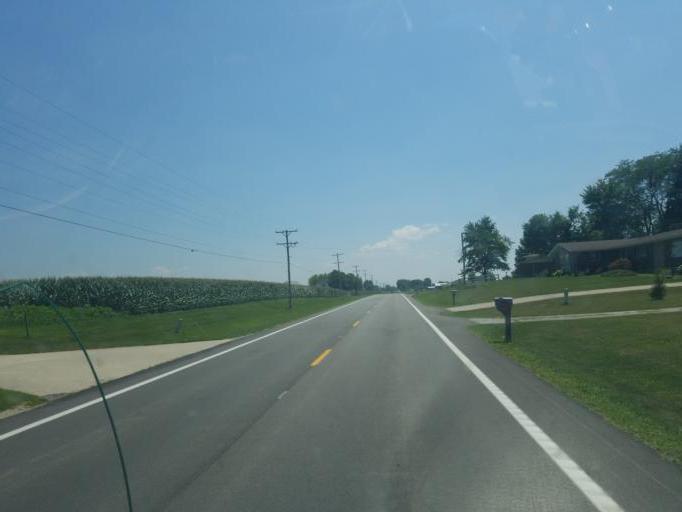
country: US
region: Ohio
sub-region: Shelby County
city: Botkins
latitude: 40.4789
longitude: -84.1836
